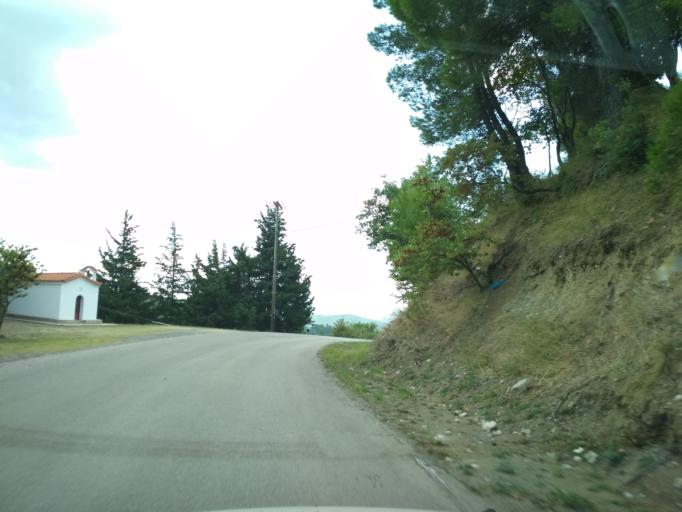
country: GR
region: Central Greece
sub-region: Nomos Evvoias
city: Roviai
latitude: 38.8471
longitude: 23.2825
